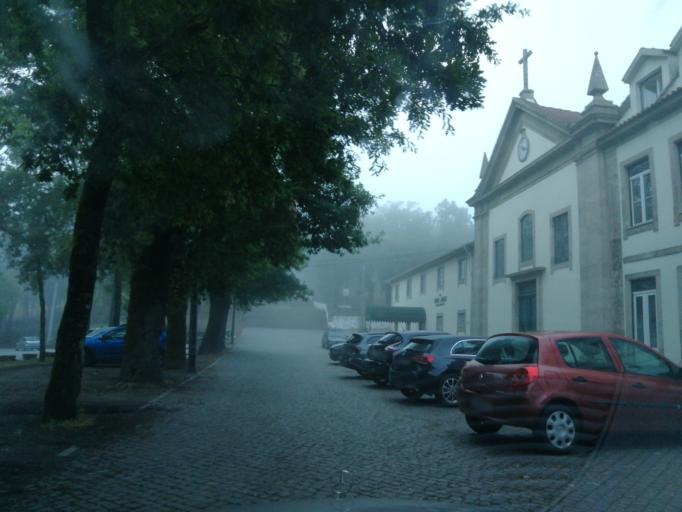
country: PT
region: Braga
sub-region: Braga
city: Braga
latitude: 41.5206
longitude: -8.3896
